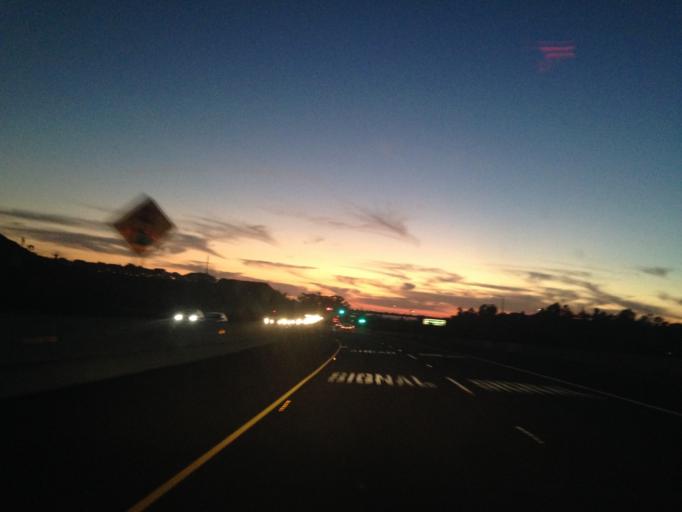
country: US
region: California
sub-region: San Diego County
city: Oceanside
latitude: 33.2118
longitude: -117.3760
